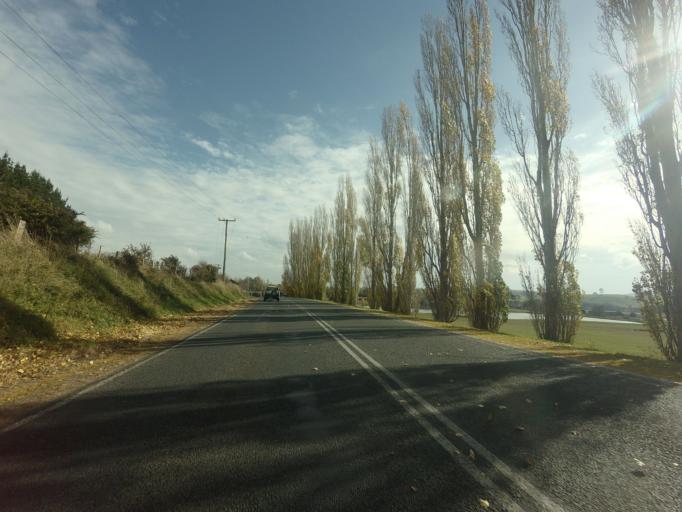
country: AU
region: Tasmania
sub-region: Meander Valley
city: Deloraine
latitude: -41.5244
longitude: 146.6718
